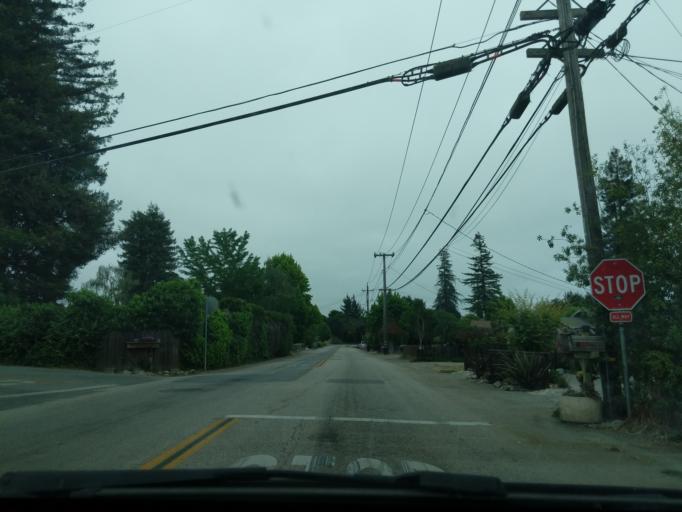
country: US
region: California
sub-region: Santa Cruz County
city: Interlaken
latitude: 36.9341
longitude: -121.7380
